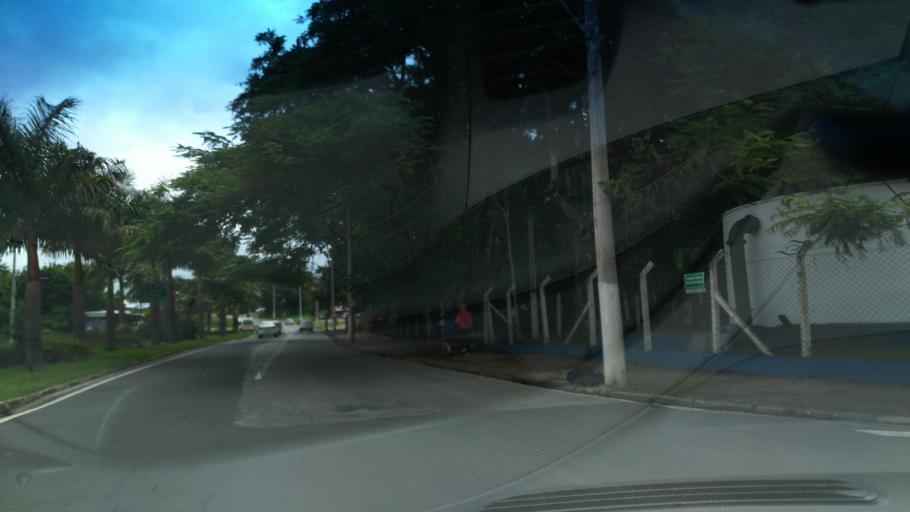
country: BR
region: Sao Paulo
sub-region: Valinhos
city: Valinhos
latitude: -22.9564
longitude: -46.9852
